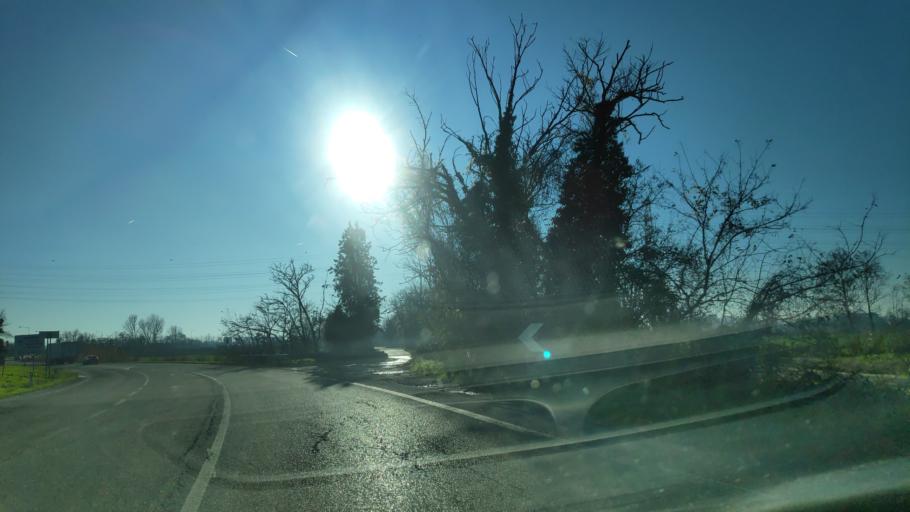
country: IT
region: Lombardy
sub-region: Citta metropolitana di Milano
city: Colturano
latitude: 45.3738
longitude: 9.3359
